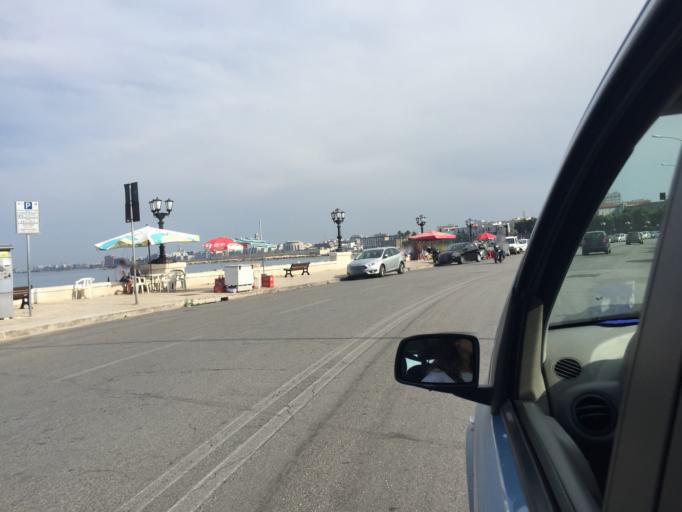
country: IT
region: Apulia
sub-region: Provincia di Bari
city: Bari
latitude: 41.1330
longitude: 16.8716
